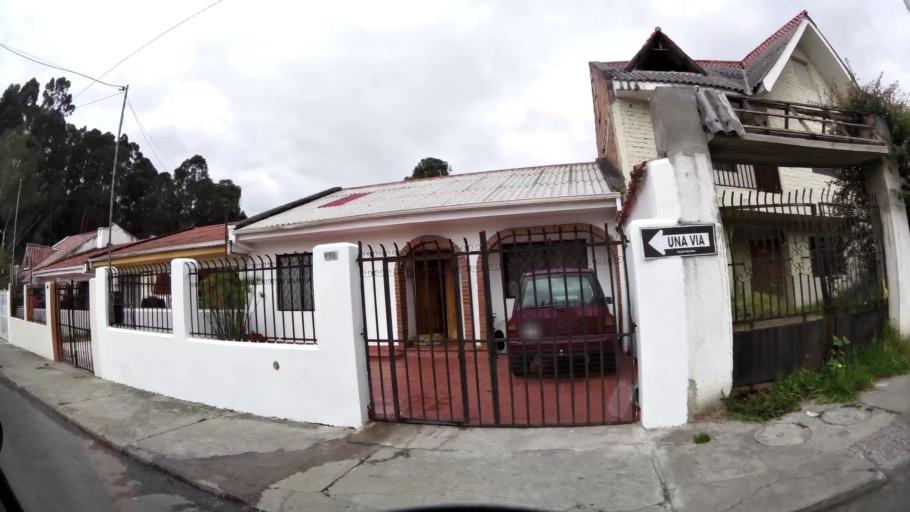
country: EC
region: Azuay
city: Cuenca
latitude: -2.9141
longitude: -79.0070
